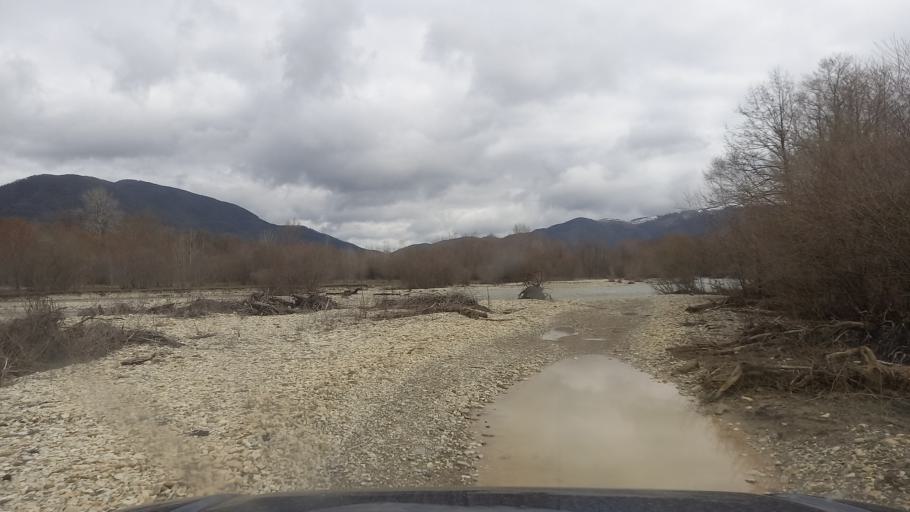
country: RU
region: Krasnodarskiy
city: Pshada
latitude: 44.4860
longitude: 38.4093
